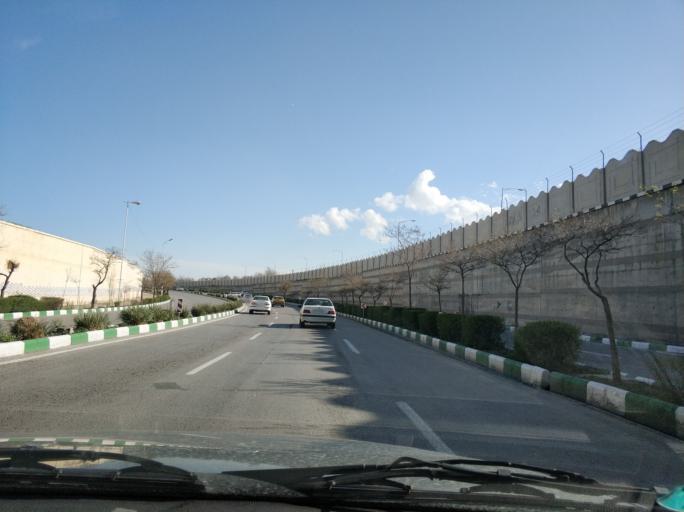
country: IR
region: Razavi Khorasan
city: Mashhad
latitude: 36.3050
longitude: 59.6276
